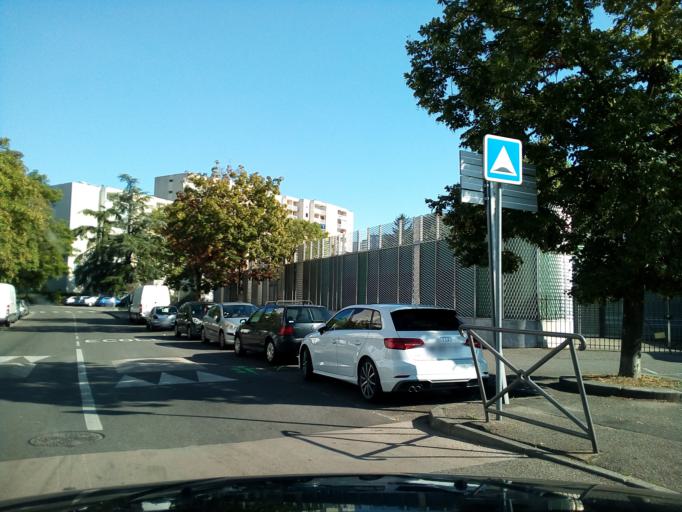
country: FR
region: Rhone-Alpes
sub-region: Departement du Rhone
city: Vaulx-en-Velin
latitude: 45.7855
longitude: 4.9133
